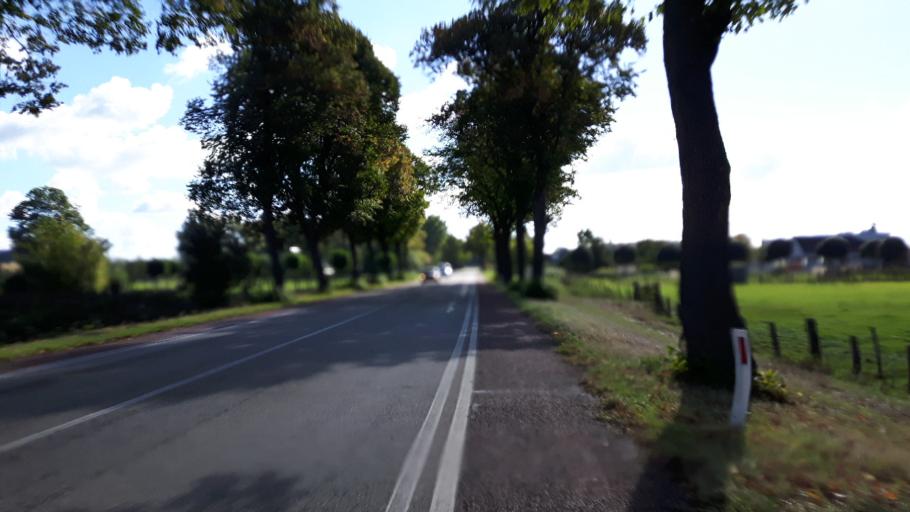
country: NL
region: Gelderland
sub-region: Gemeente Culemborg
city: Culemborg
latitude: 51.9407
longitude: 5.2473
